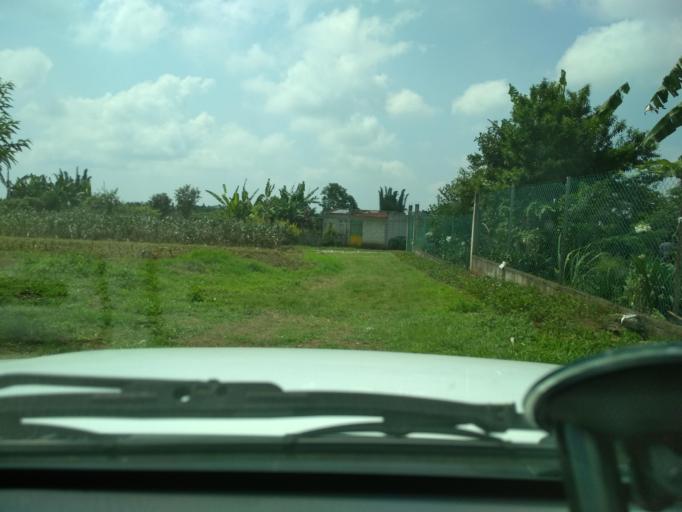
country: MX
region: Veracruz
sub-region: Fortin
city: Santa Lucia Potrerillo
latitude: 18.9665
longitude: -97.0264
